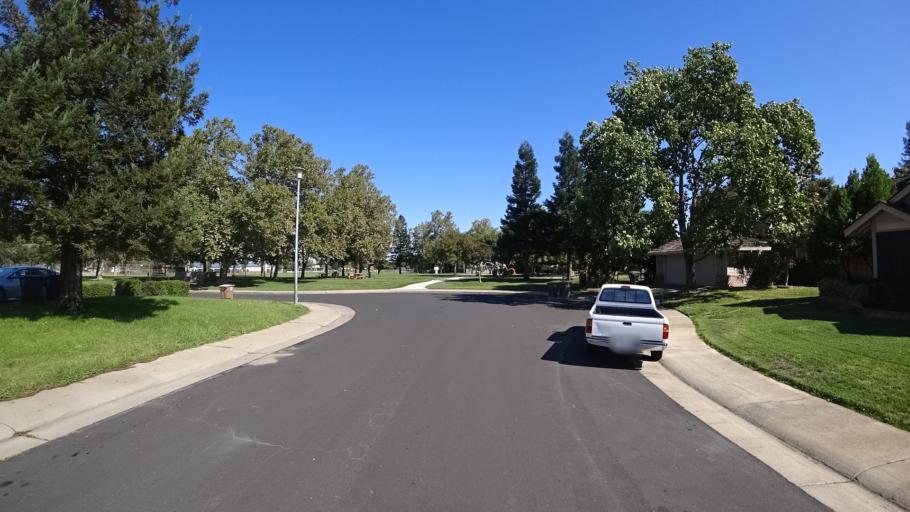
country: US
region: California
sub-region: Sacramento County
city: Laguna
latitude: 38.4267
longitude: -121.4352
